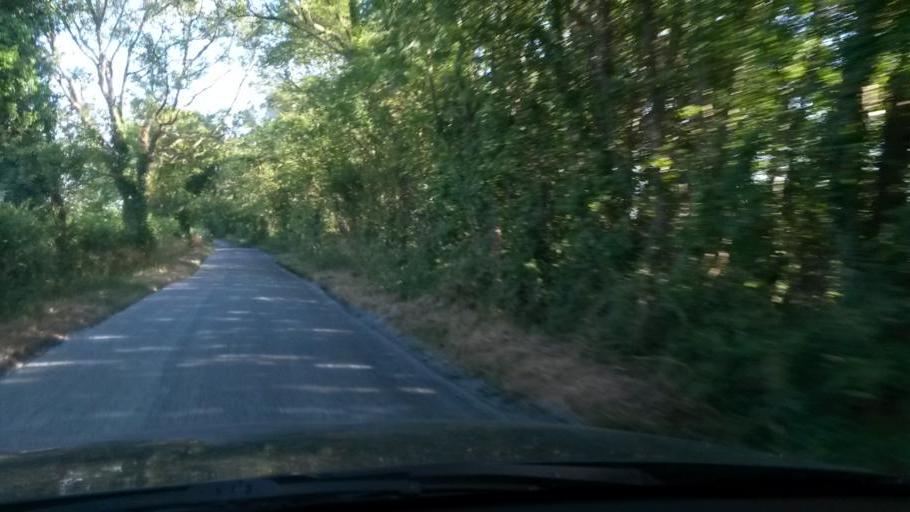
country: IE
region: Leinster
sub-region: An Mhi
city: Ashbourne
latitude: 53.4960
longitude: -6.3063
